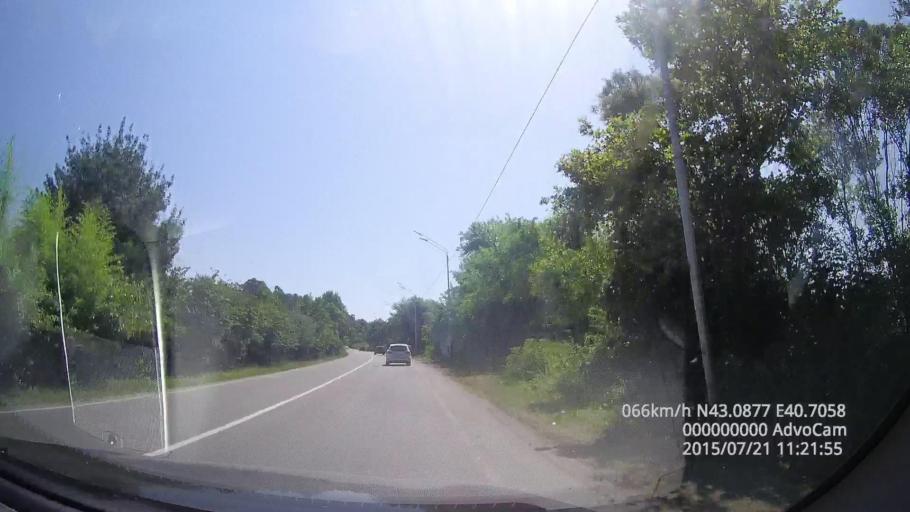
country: GE
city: P'rimorsk'oe
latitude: 43.0876
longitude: 40.7062
